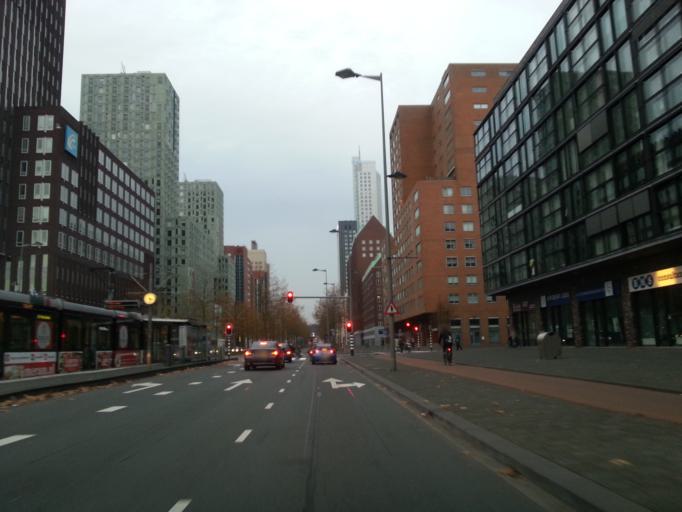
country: NL
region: South Holland
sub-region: Gemeente Rotterdam
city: Rotterdam
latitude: 51.9059
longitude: 4.4991
